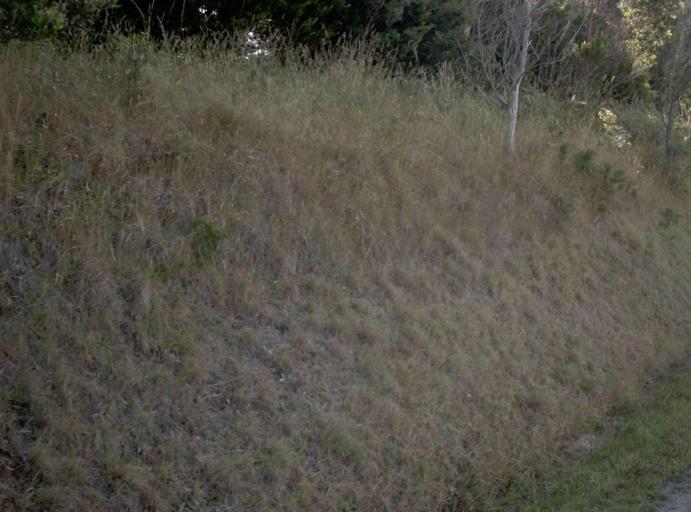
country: AU
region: Victoria
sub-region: Latrobe
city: Morwell
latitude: -38.4150
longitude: 146.2795
